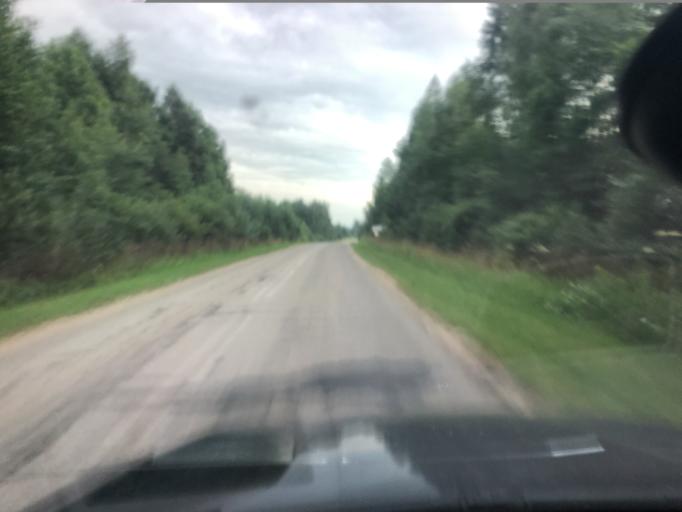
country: RU
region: Jaroslavl
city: Pereslavl'-Zalesskiy
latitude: 57.0121
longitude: 38.9681
